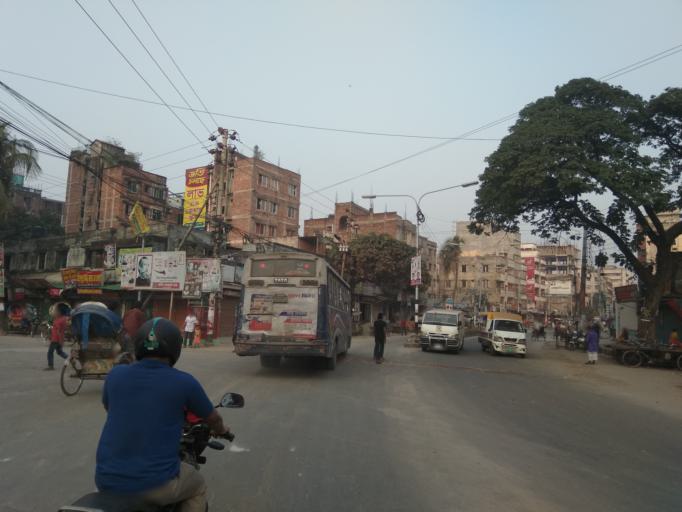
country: BD
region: Dhaka
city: Tungi
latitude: 23.8149
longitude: 90.3625
